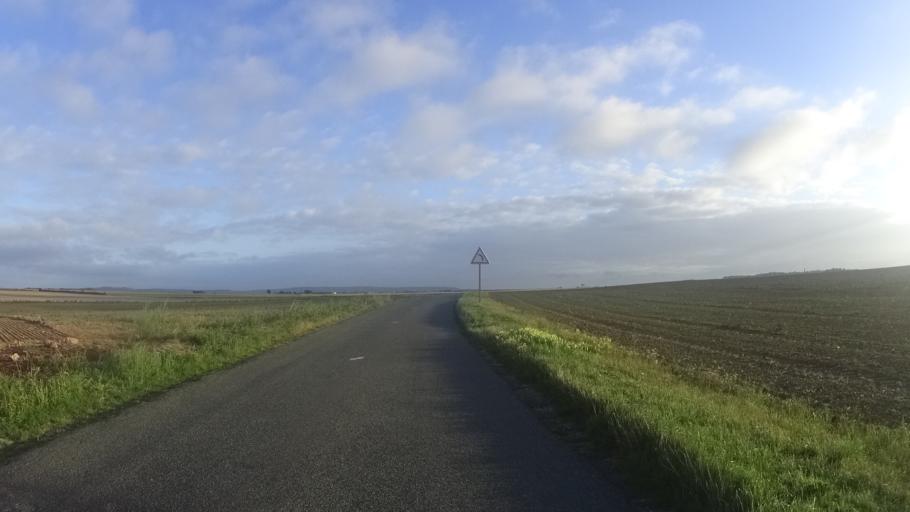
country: FR
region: Picardie
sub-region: Departement de l'Oise
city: Chamant
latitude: 49.1875
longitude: 2.6718
